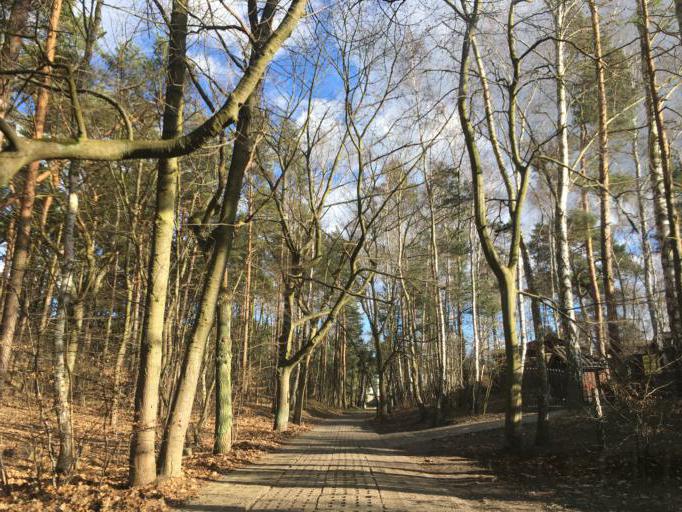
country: PL
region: Pomeranian Voivodeship
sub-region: Powiat gdanski
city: Cedry Wielkie
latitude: 54.3455
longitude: 18.8336
